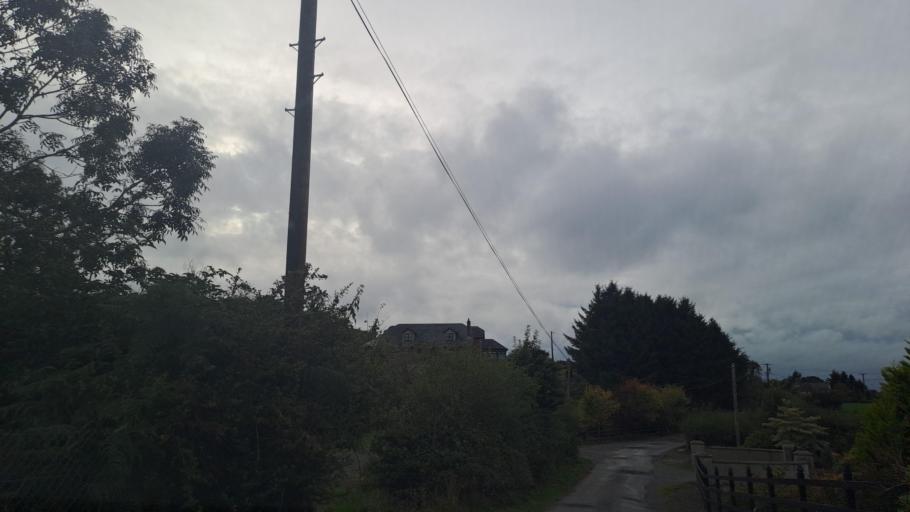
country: IE
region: Ulster
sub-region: An Cabhan
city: Bailieborough
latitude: 53.9827
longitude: -6.8906
